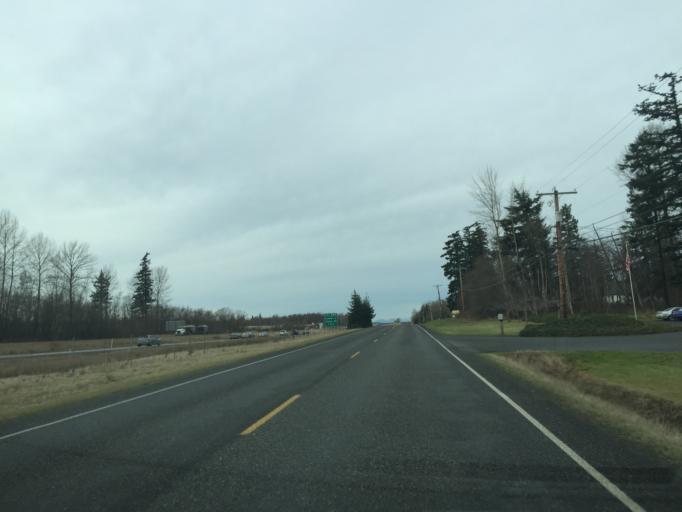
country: US
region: Washington
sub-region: Whatcom County
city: Marietta-Alderwood
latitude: 48.8010
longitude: -122.5316
